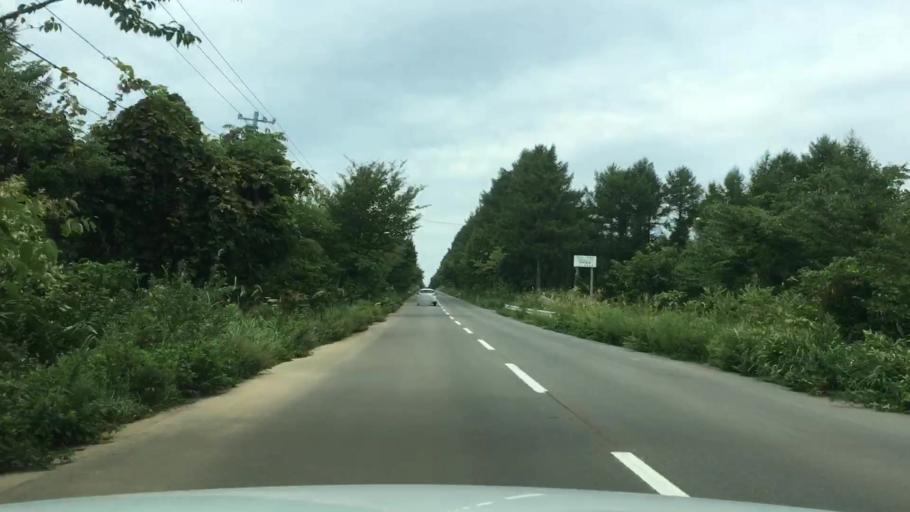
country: JP
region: Aomori
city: Shimokizukuri
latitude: 40.7094
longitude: 140.3370
